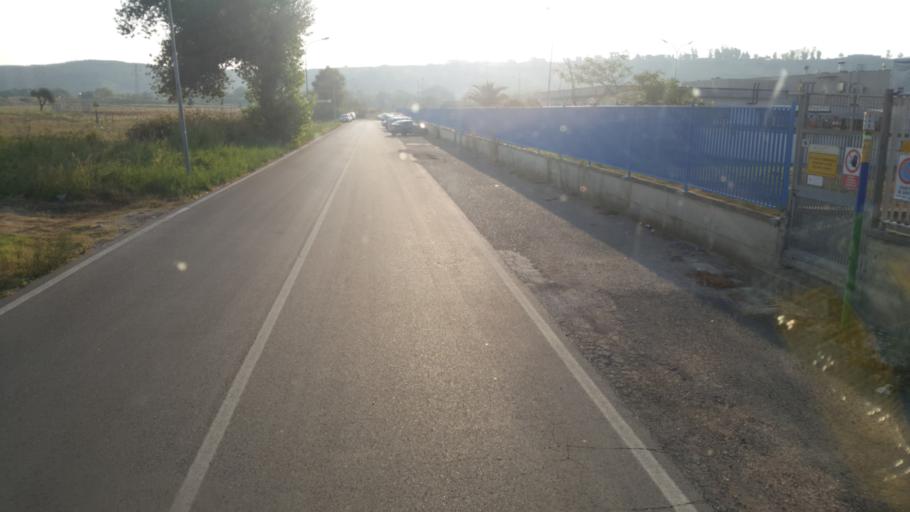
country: IT
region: Molise
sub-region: Provincia di Campobasso
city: Portocannone
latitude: 41.9458
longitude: 15.0044
